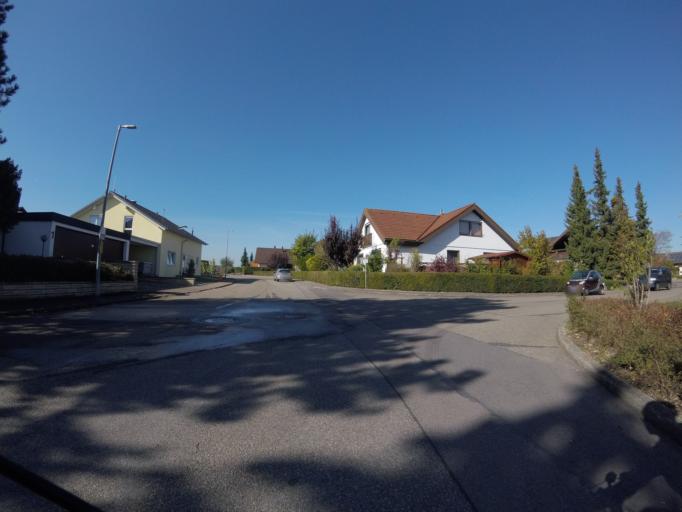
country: DE
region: Baden-Wuerttemberg
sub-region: Regierungsbezirk Stuttgart
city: Sersheim
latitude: 48.9650
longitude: 9.0163
